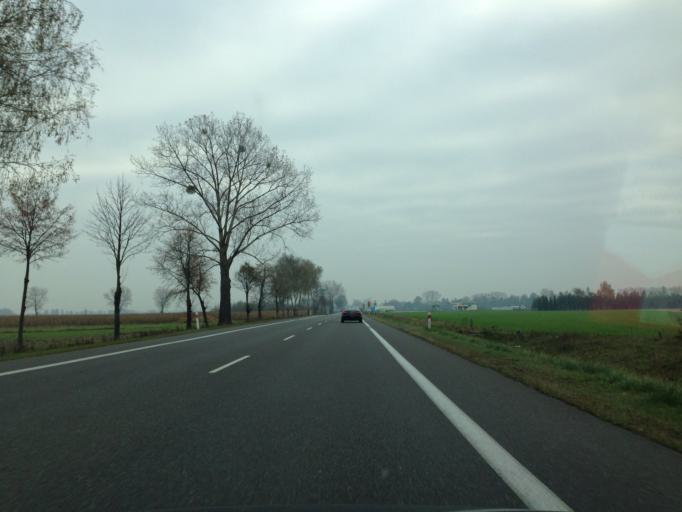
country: PL
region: Masovian Voivodeship
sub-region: Powiat plocki
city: Drobin
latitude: 52.7067
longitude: 20.0325
